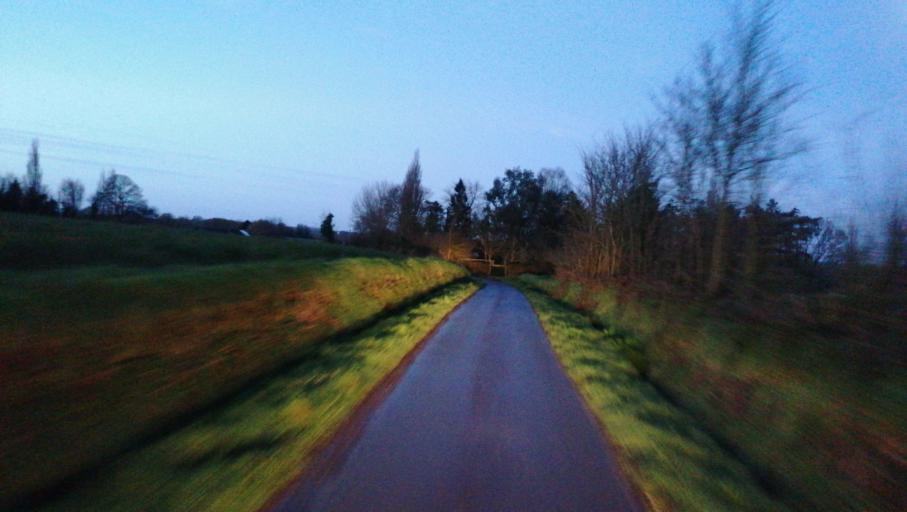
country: FR
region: Brittany
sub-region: Departement des Cotes-d'Armor
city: Lanvollon
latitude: 48.6636
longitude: -2.9672
